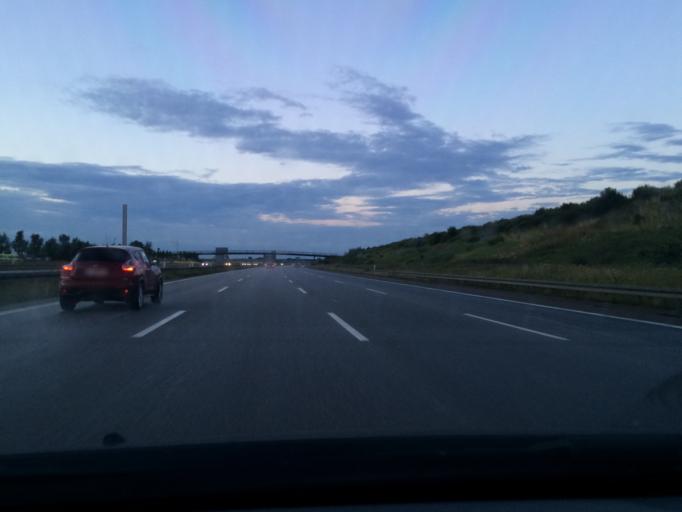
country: DK
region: Zealand
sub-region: Greve Kommune
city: Greve
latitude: 55.5876
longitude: 12.2670
